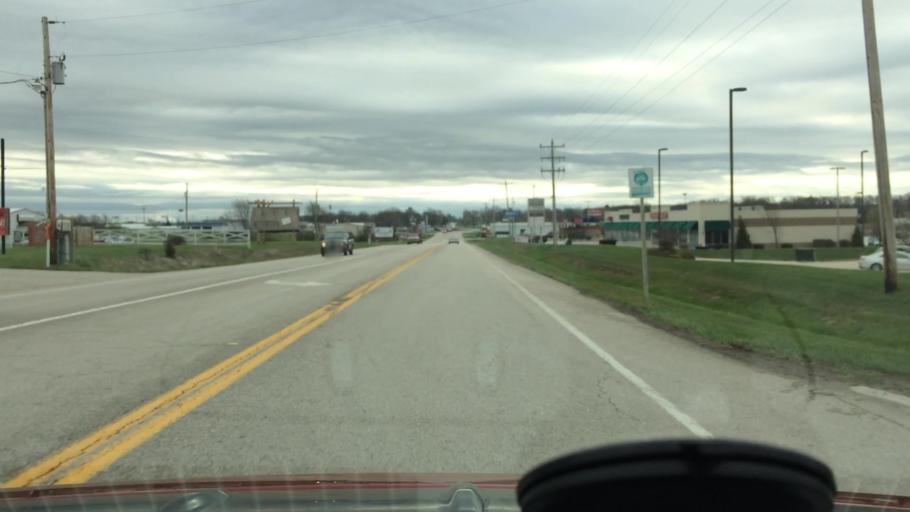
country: US
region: Missouri
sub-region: Webster County
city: Marshfield
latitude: 37.3401
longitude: -92.9422
